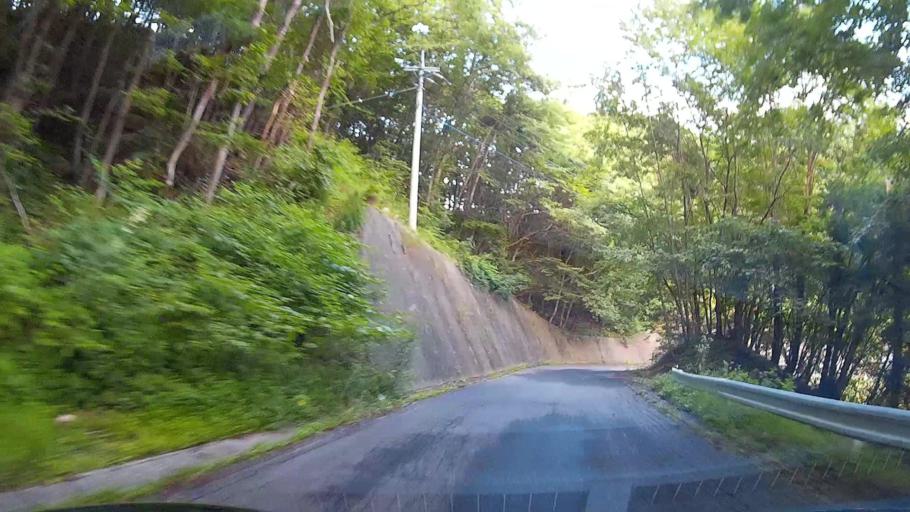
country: JP
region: Gunma
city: Nakanojomachi
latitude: 36.6282
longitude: 138.6250
